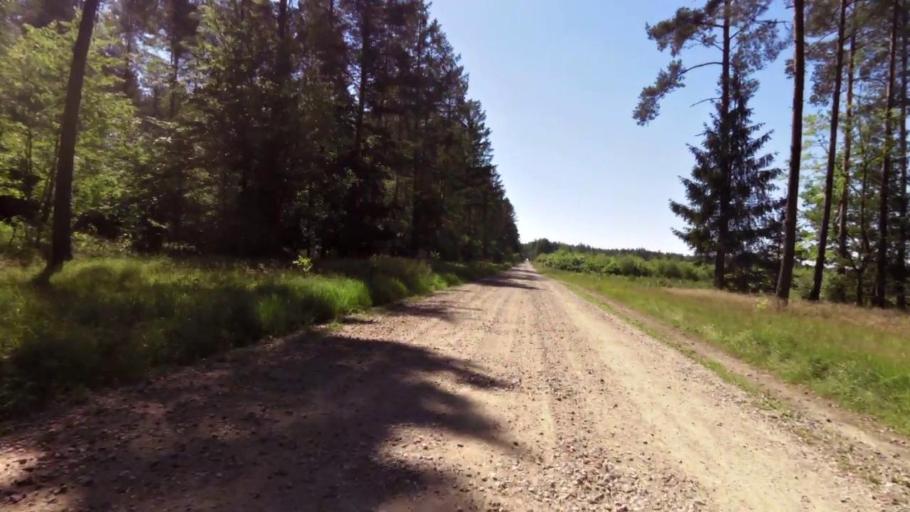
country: PL
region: West Pomeranian Voivodeship
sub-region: Powiat swidwinski
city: Rabino
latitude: 53.8998
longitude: 16.0082
